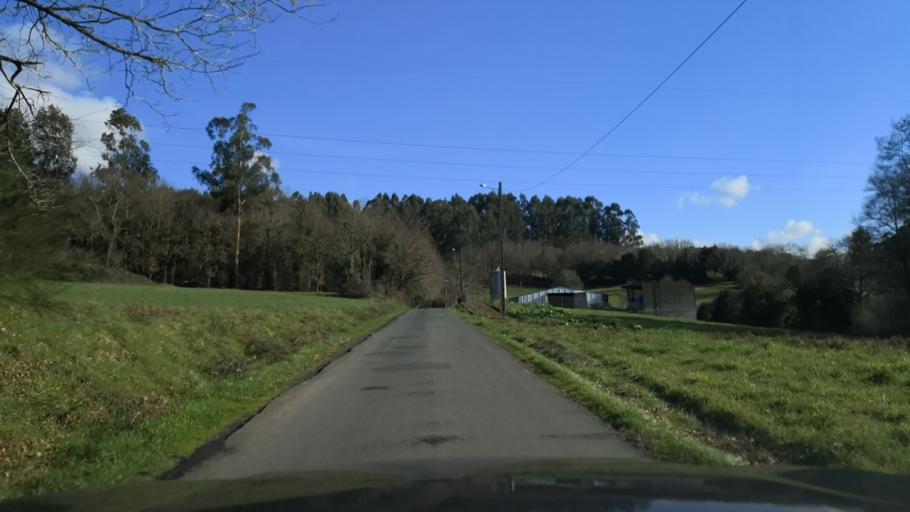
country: ES
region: Galicia
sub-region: Provincia da Coruna
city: Ribeira
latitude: 42.7115
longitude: -8.4328
